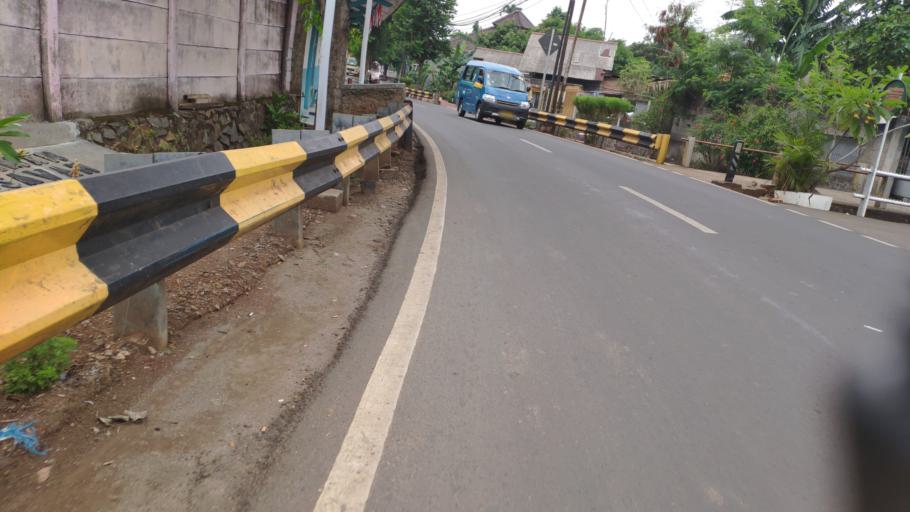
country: ID
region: West Java
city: Depok
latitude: -6.3460
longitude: 106.8228
